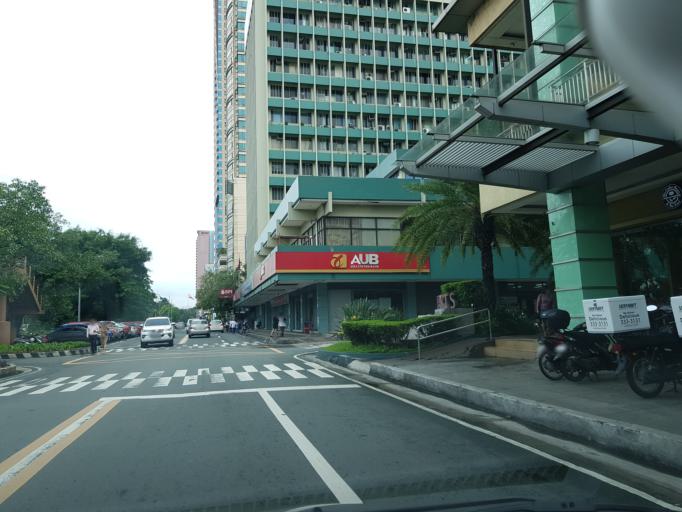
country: PH
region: Metro Manila
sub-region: City of Manila
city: Port Area
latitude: 14.5748
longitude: 120.9805
